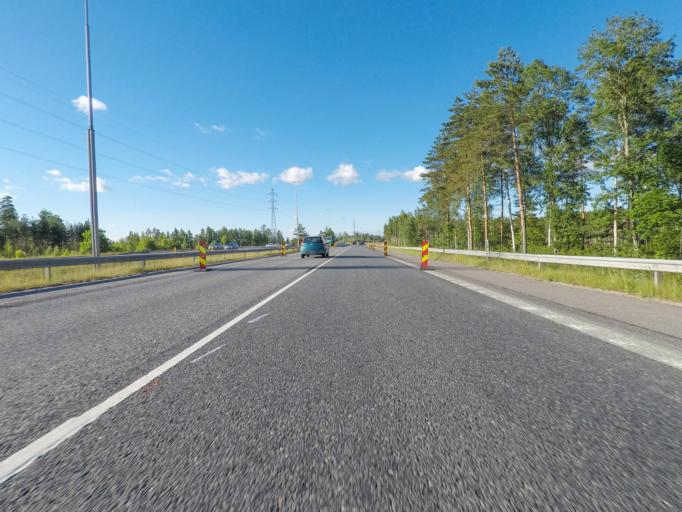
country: FI
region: Uusimaa
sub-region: Helsinki
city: Vantaa
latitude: 60.3054
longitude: 25.0989
